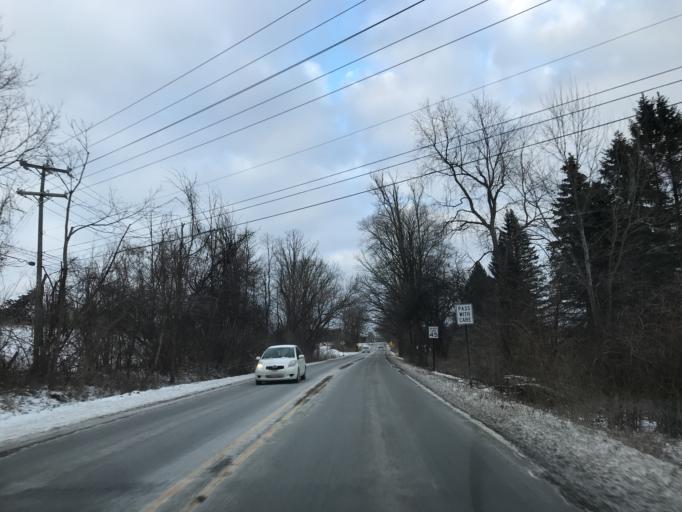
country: US
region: Michigan
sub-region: Washtenaw County
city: Ann Arbor
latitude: 42.2951
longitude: -83.6688
